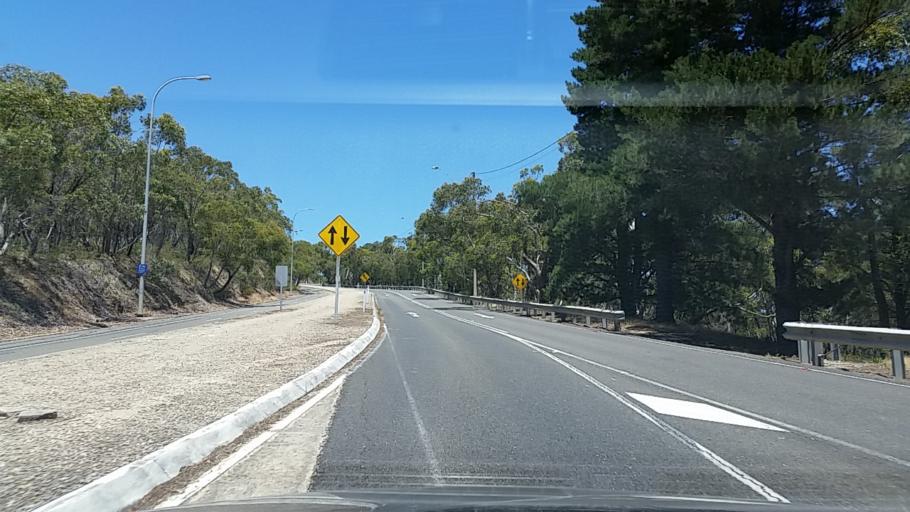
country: AU
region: South Australia
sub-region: Adelaide Hills
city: Crafers
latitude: -34.9800
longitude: 138.6867
